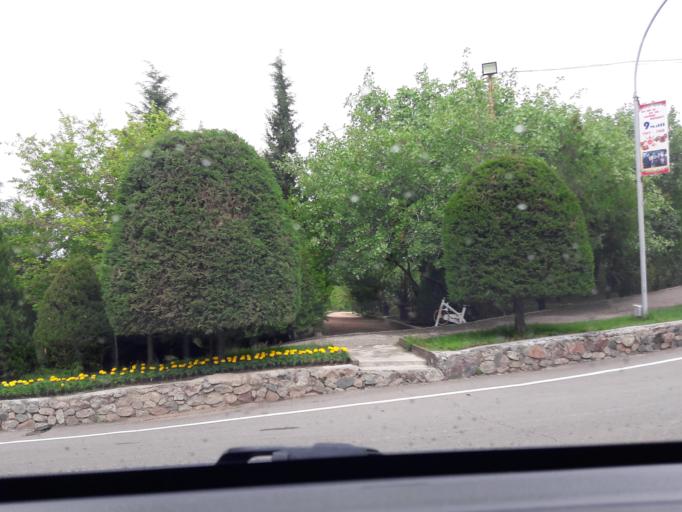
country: TJ
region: Dushanbe
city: Dushanbe
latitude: 38.5794
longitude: 68.8108
